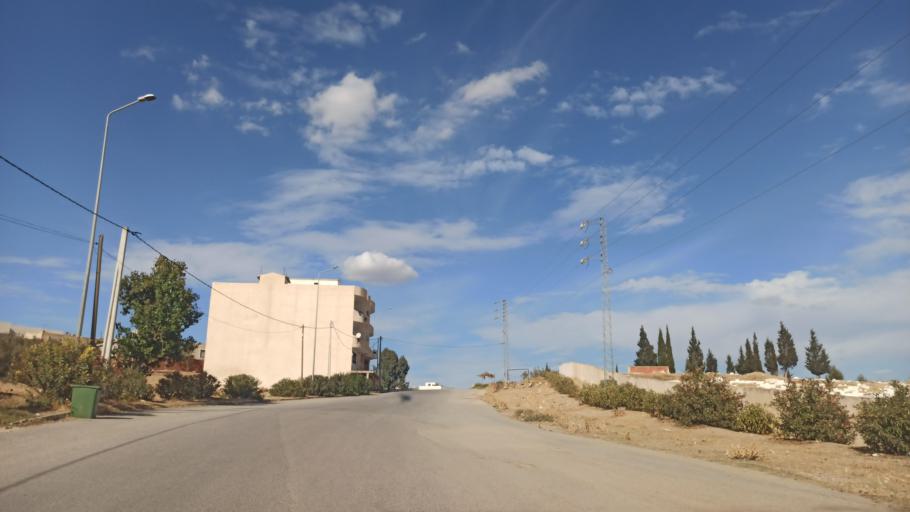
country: TN
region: Zaghwan
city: Zaghouan
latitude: 36.3455
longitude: 10.2071
